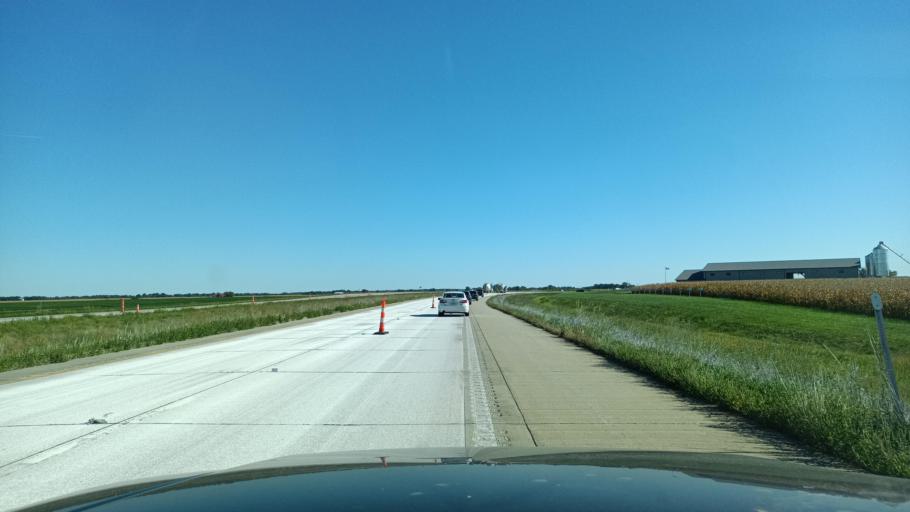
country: US
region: Missouri
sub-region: Randolph County
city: Moberly
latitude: 39.5187
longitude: -92.4355
